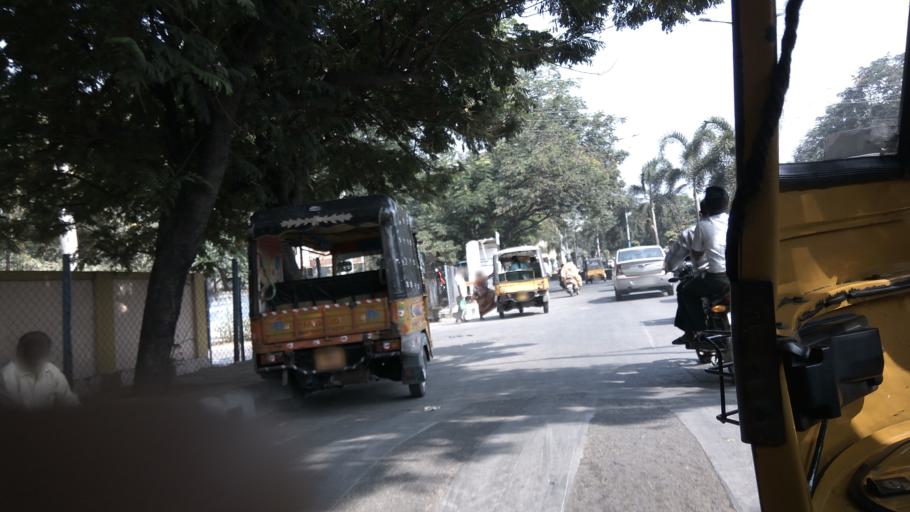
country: IN
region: Andhra Pradesh
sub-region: Chittoor
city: Tirupati
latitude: 13.6331
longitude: 79.4133
